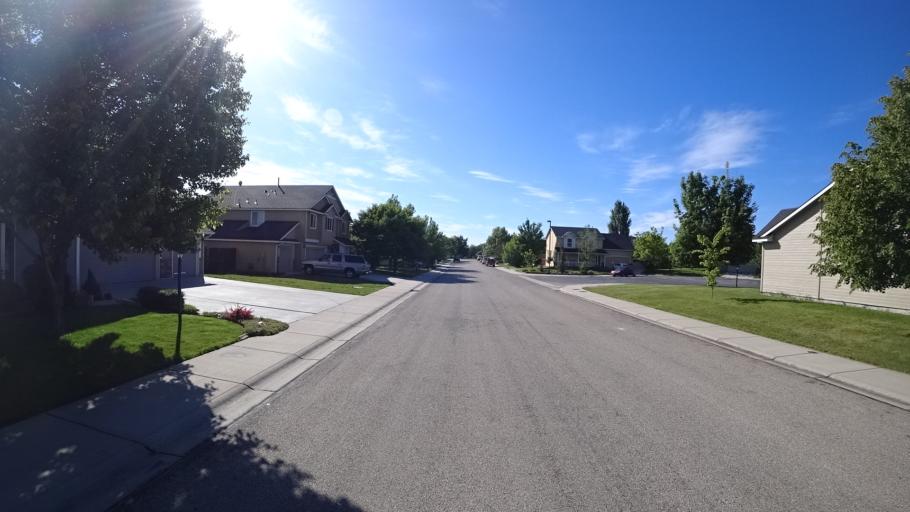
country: US
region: Idaho
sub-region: Ada County
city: Garden City
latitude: 43.5700
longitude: -116.2777
